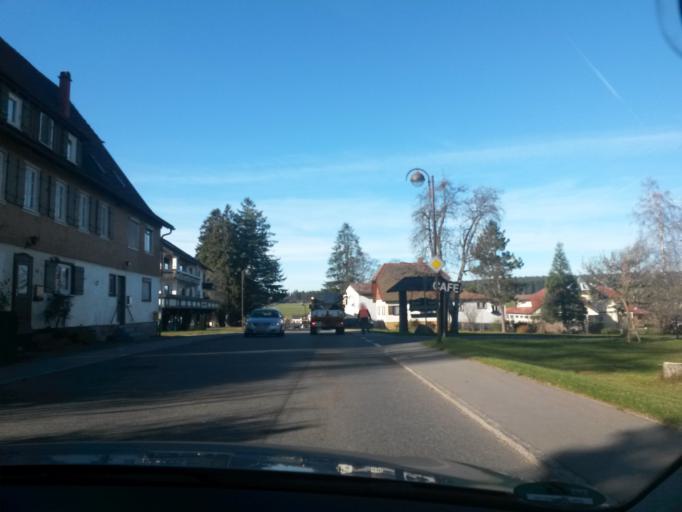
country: DE
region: Baden-Wuerttemberg
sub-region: Karlsruhe Region
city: Baiersbronn
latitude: 48.5906
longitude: 8.4196
